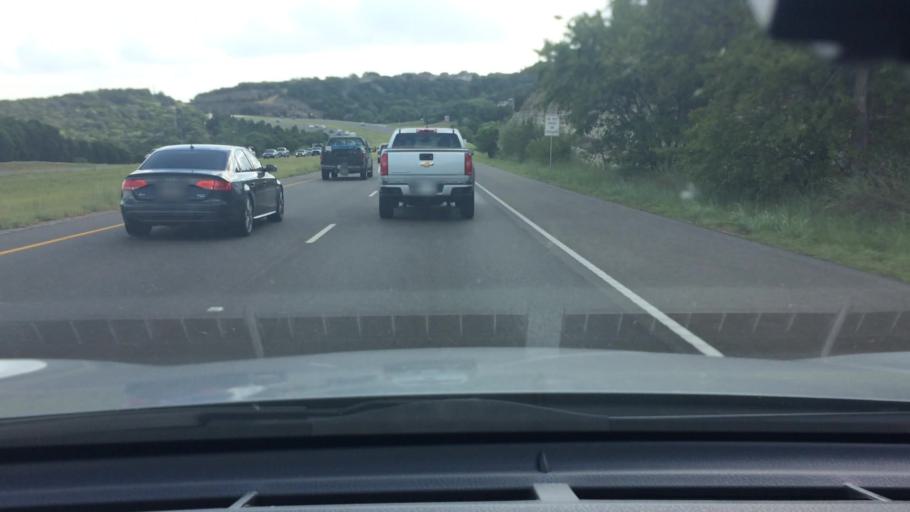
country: US
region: Texas
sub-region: Travis County
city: West Lake Hills
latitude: 30.3199
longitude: -97.8184
